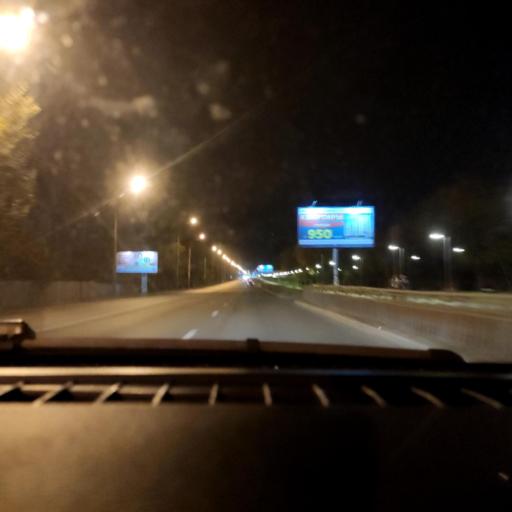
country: RU
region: Voronezj
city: Voronezh
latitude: 51.6659
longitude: 39.2676
